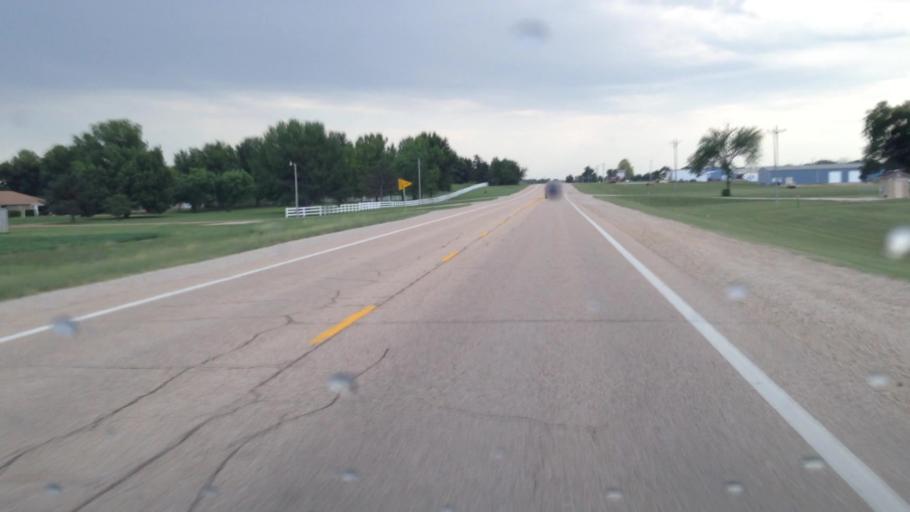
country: US
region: Kansas
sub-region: Coffey County
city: Burlington
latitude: 38.1823
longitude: -95.7388
